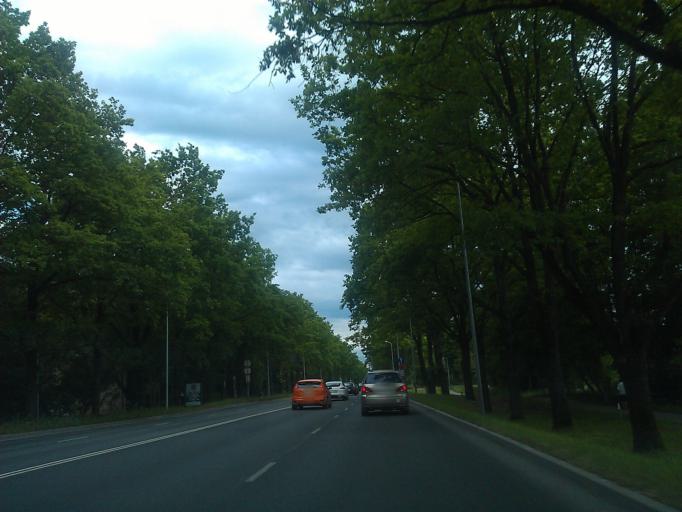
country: LV
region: Marupe
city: Marupe
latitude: 56.9041
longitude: 24.0817
